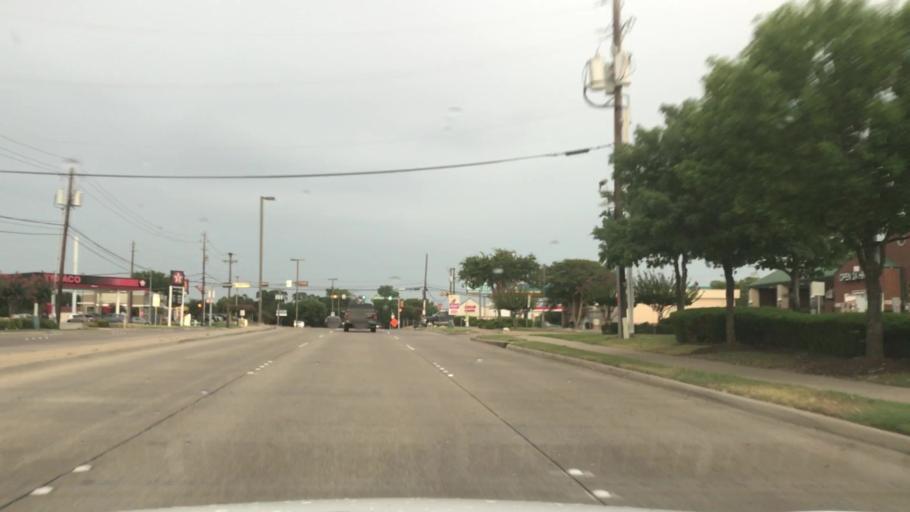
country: US
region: Texas
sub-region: Dallas County
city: Mesquite
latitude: 32.7467
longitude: -96.5982
